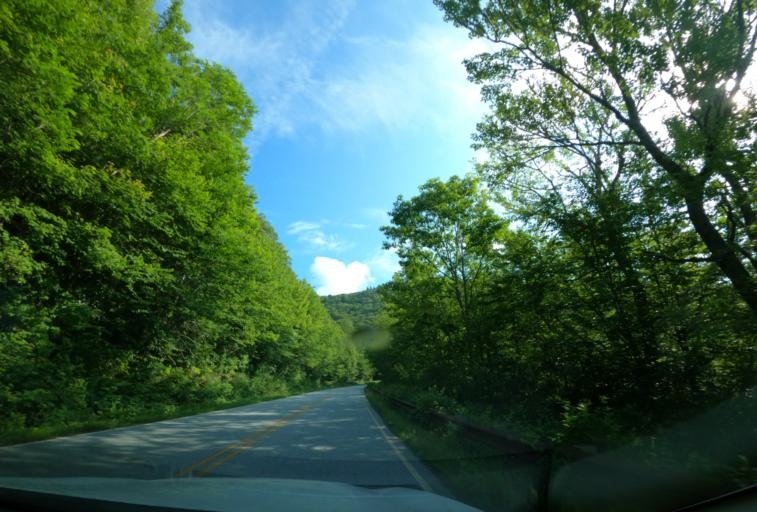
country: US
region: North Carolina
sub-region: Transylvania County
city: Brevard
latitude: 35.2870
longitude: -82.9196
